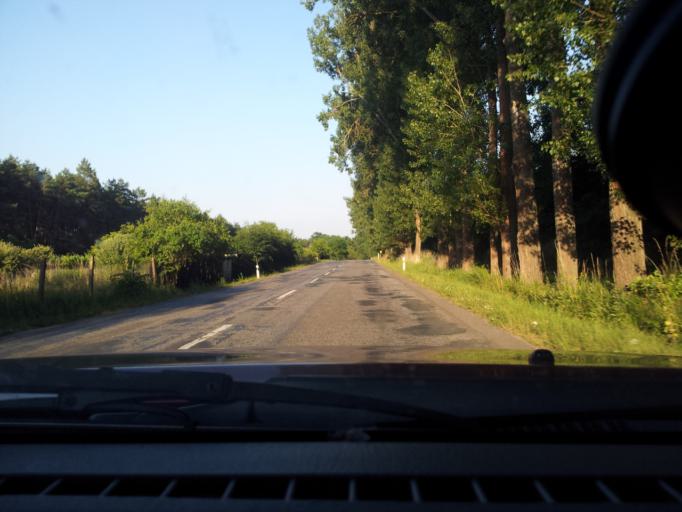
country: CZ
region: South Moravian
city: Dubnany
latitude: 48.8822
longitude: 17.1080
